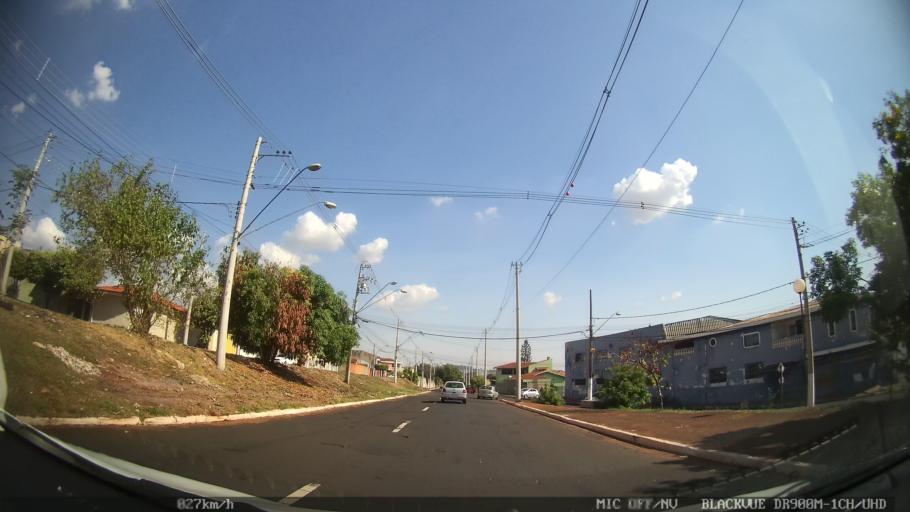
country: BR
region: Sao Paulo
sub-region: Ribeirao Preto
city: Ribeirao Preto
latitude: -21.1924
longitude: -47.8463
